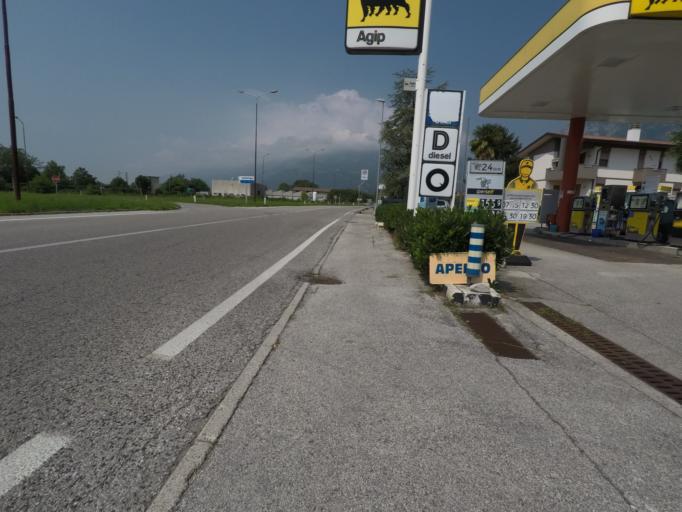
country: IT
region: Friuli Venezia Giulia
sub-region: Provincia di Pordenone
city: Vajont
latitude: 46.1605
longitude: 12.6862
